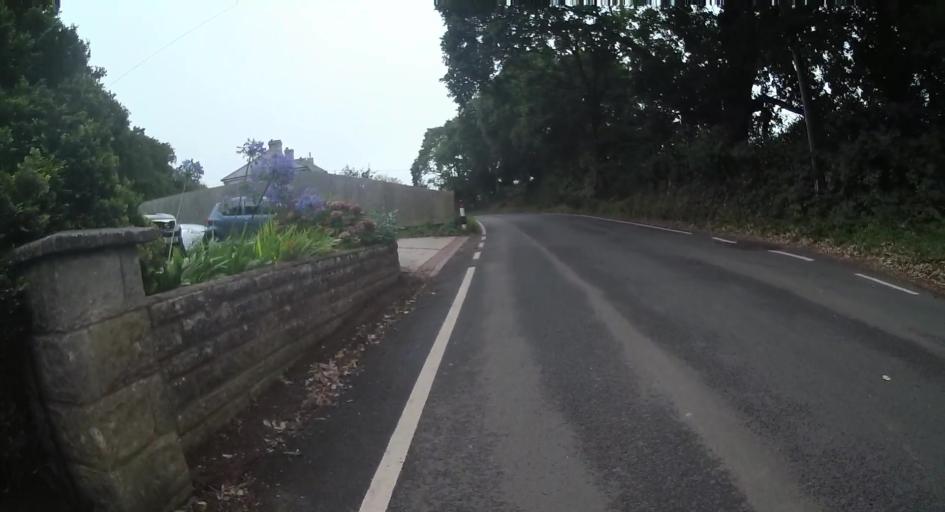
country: GB
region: England
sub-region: Isle of Wight
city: Newchurch
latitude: 50.6579
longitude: -1.1979
